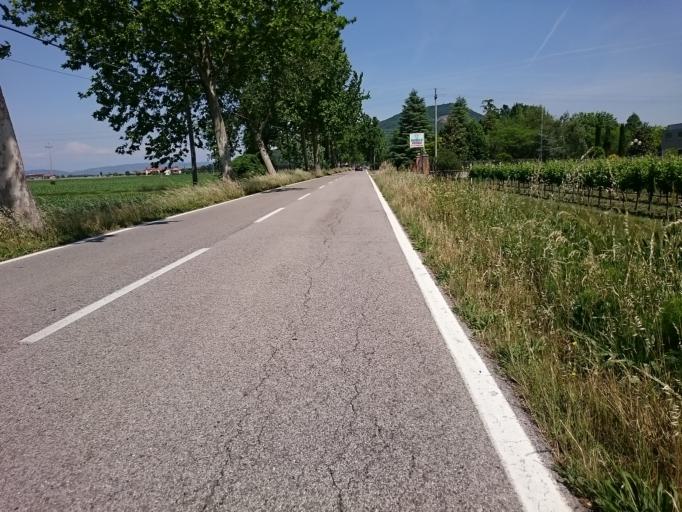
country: IT
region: Veneto
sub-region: Provincia di Padova
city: Lozzo Atestino
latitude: 45.2701
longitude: 11.6163
